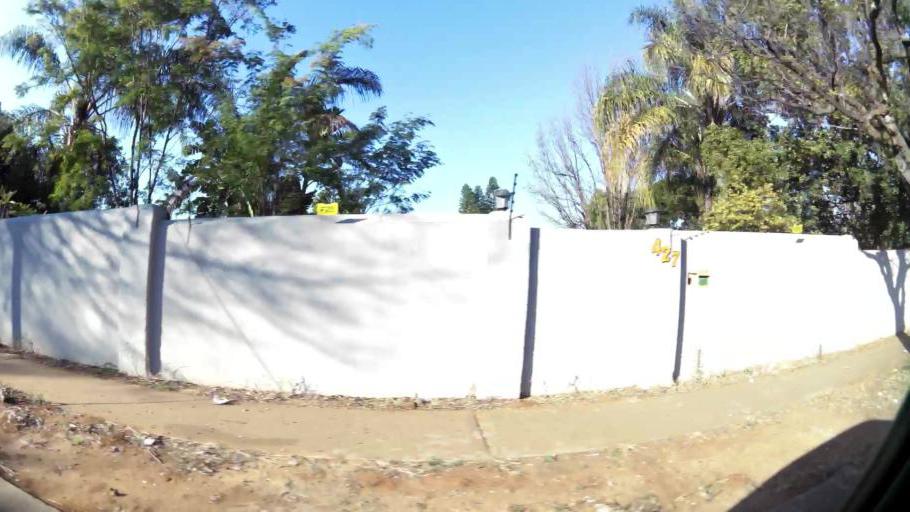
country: ZA
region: Gauteng
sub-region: City of Tshwane Metropolitan Municipality
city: Pretoria
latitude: -25.6994
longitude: 28.1964
